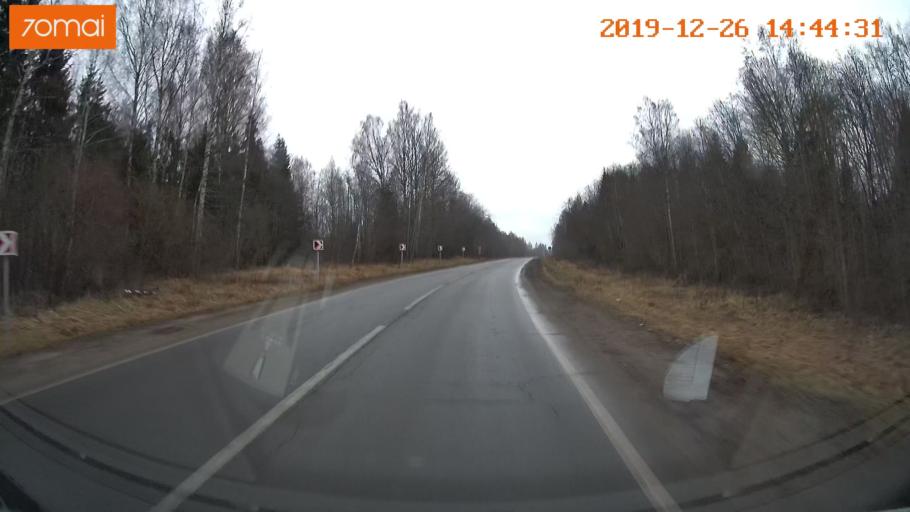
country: RU
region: Jaroslavl
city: Poshekhon'ye
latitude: 58.3472
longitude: 39.0511
